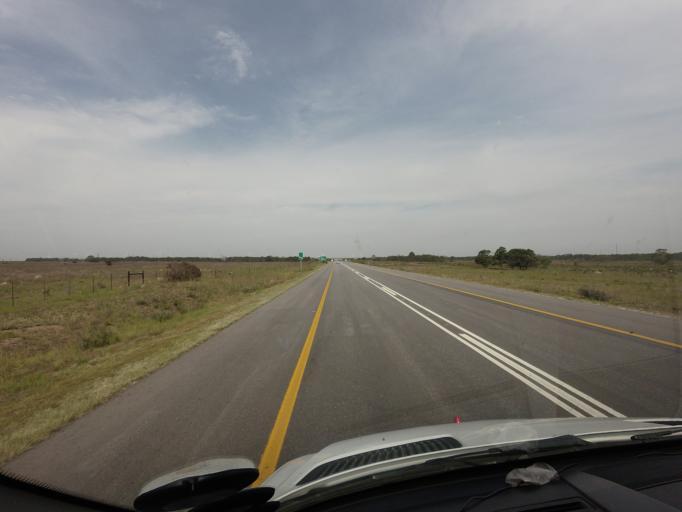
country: ZA
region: Eastern Cape
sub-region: Cacadu District Municipality
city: Kruisfontein
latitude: -34.0045
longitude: 24.7719
